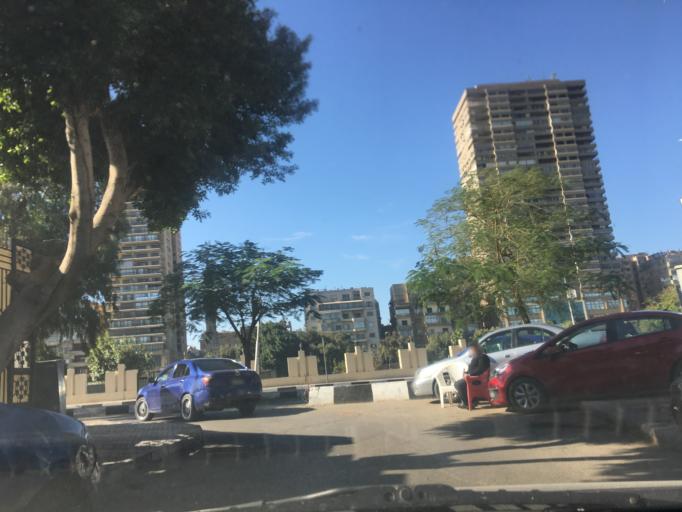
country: EG
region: Muhafazat al Qahirah
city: Cairo
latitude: 30.0463
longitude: 31.2203
